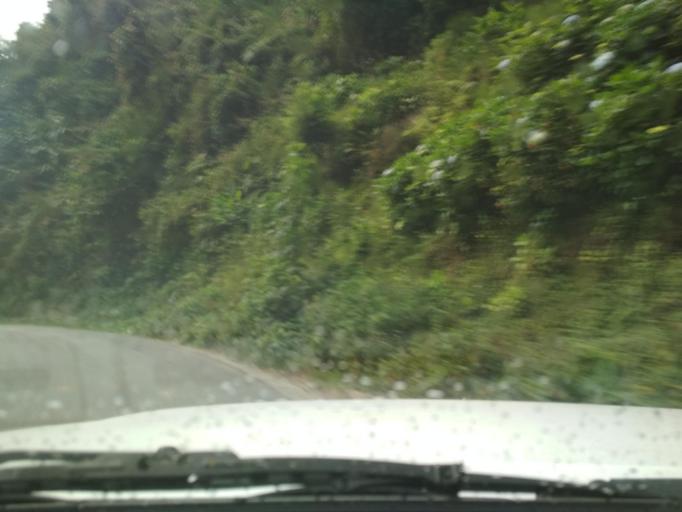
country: MX
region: Veracruz
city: La Perla
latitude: 18.9413
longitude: -97.1524
